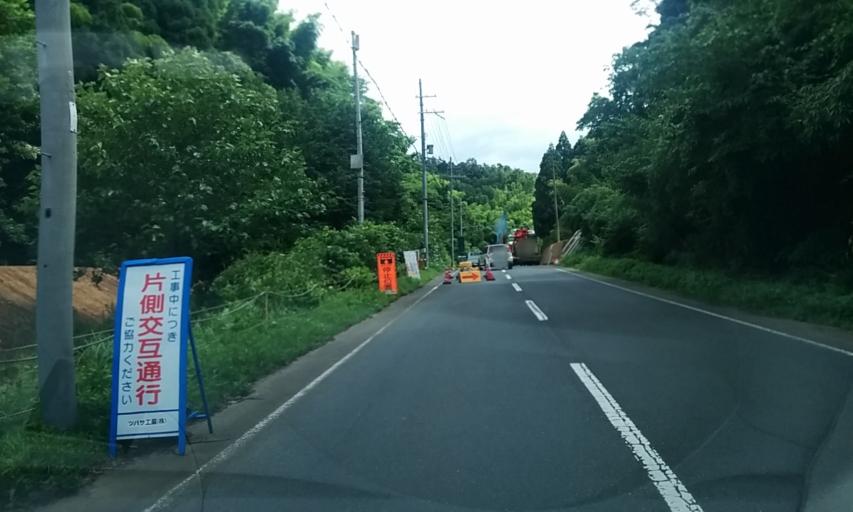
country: JP
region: Kyoto
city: Ayabe
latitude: 35.3507
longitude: 135.2737
